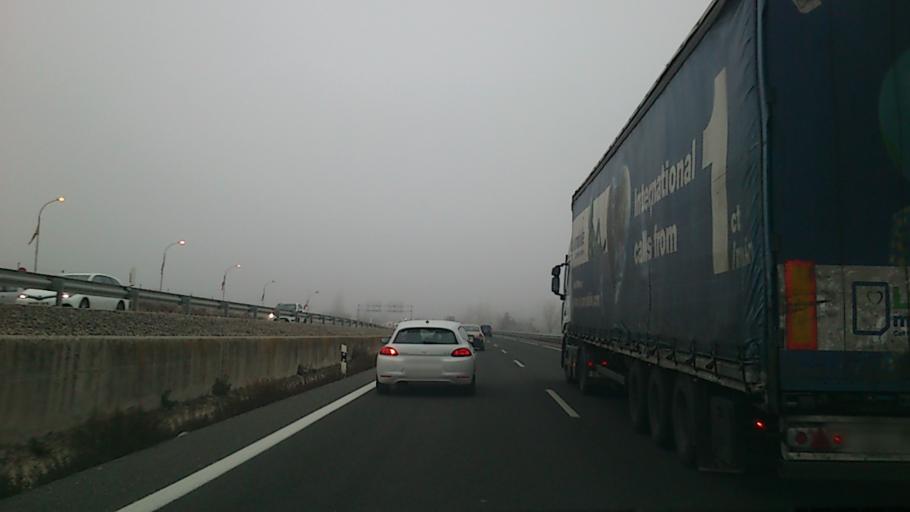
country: ES
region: Castille-La Mancha
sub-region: Provincia de Guadalajara
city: Almadrones
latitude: 40.8989
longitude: -2.7565
